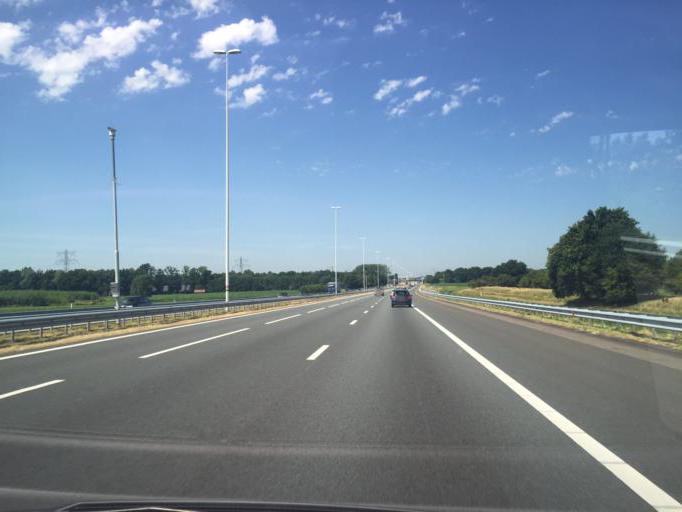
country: NL
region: Utrecht
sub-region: Gemeente Utrechtse Heuvelrug
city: Overberg
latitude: 52.0483
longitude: 5.4893
